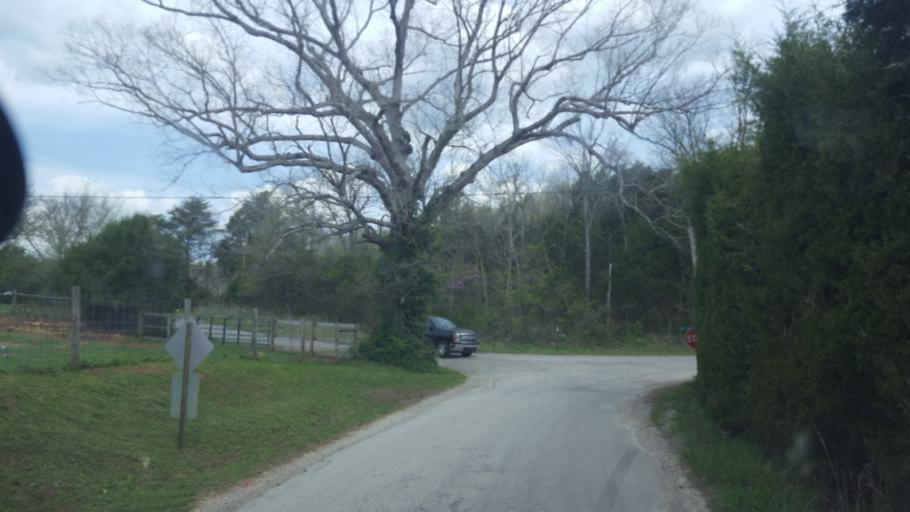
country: US
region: Kentucky
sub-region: Hart County
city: Munfordville
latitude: 37.2615
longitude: -85.9714
